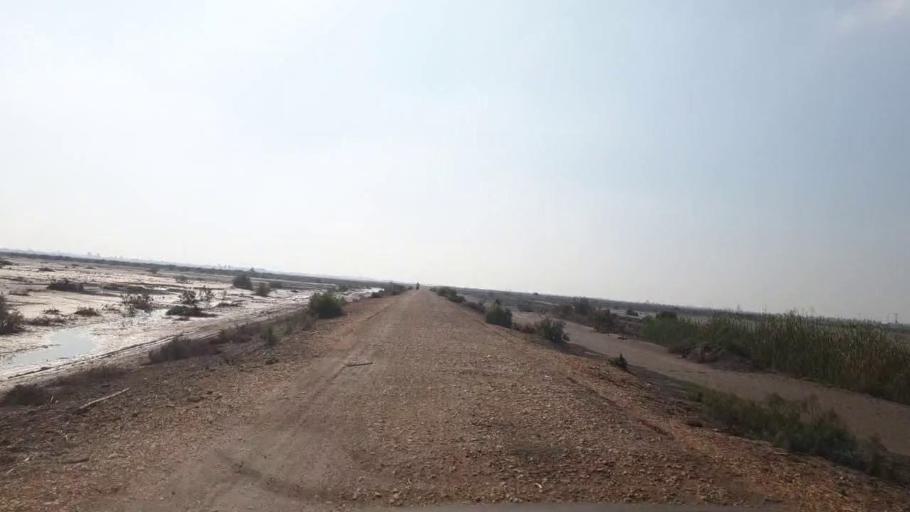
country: PK
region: Sindh
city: Sinjhoro
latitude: 26.0341
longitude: 68.7788
